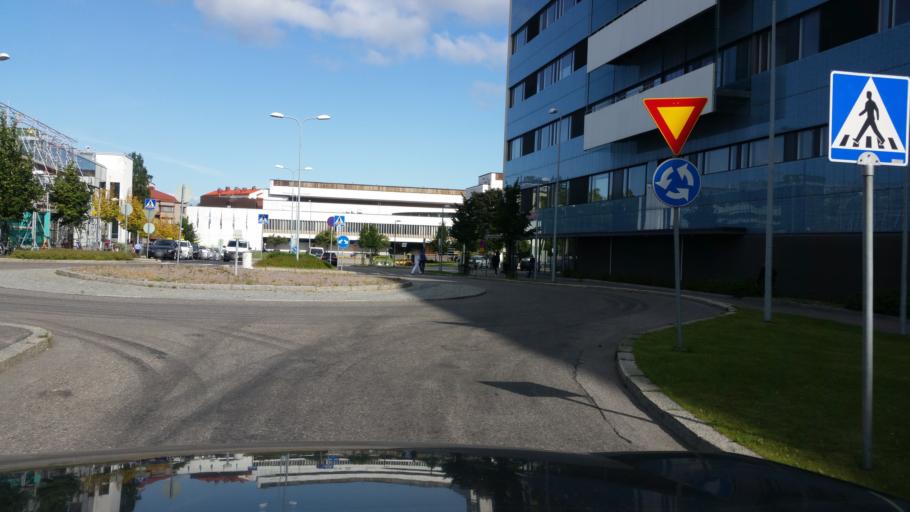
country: FI
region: Uusimaa
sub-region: Helsinki
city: Helsinki
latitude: 60.1896
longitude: 24.9067
